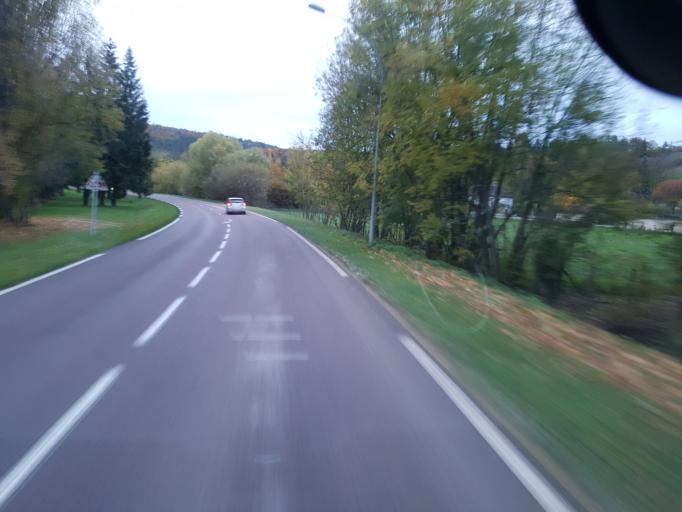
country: FR
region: Champagne-Ardenne
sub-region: Departement de l'Aube
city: Mussy-sur-Seine
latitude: 47.9765
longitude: 4.5011
